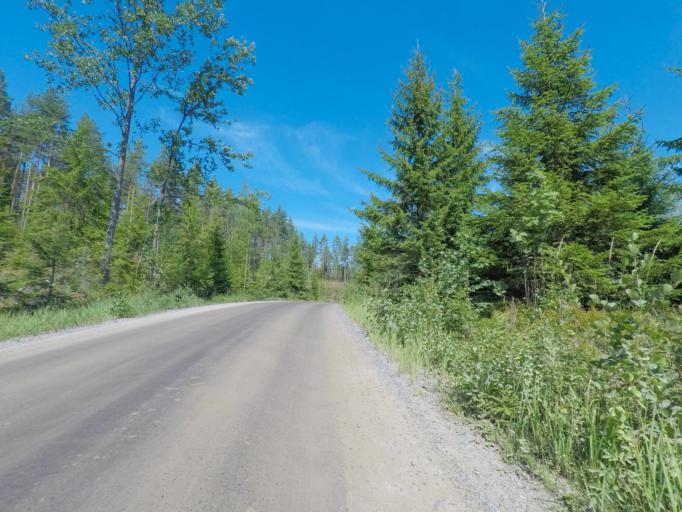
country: FI
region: Southern Savonia
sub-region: Mikkeli
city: Puumala
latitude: 61.4071
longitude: 28.0462
